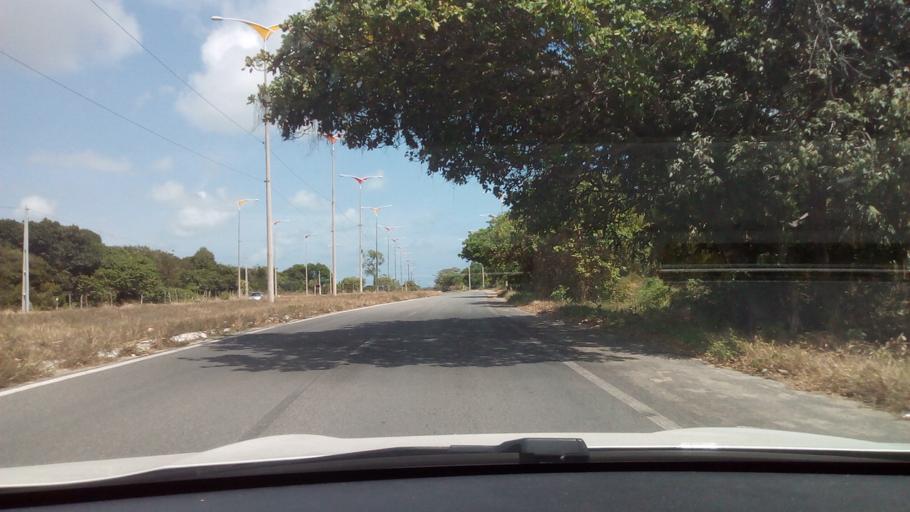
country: BR
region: Paraiba
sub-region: Joao Pessoa
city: Joao Pessoa
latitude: -7.1740
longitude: -34.8011
